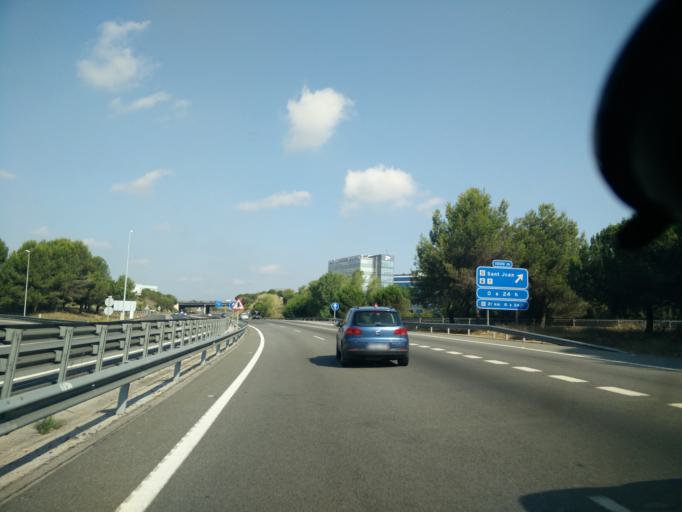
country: ES
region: Catalonia
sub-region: Provincia de Barcelona
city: Rubi
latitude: 41.4899
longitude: 2.0587
